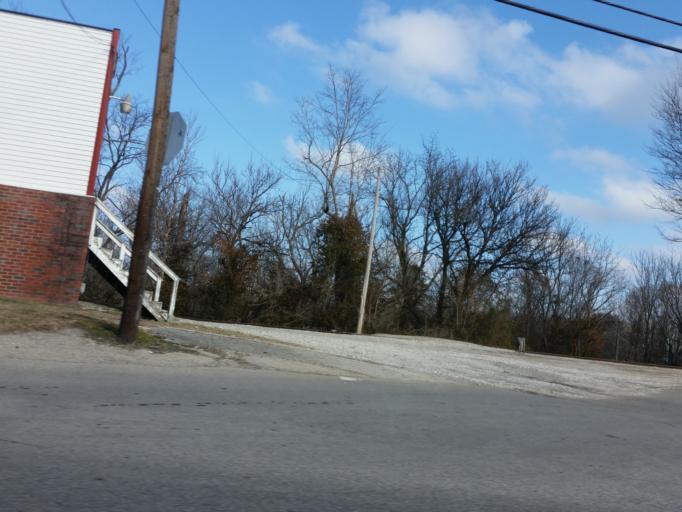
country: US
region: Indiana
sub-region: Jennings County
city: North Vernon
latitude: 38.9876
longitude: -85.6120
